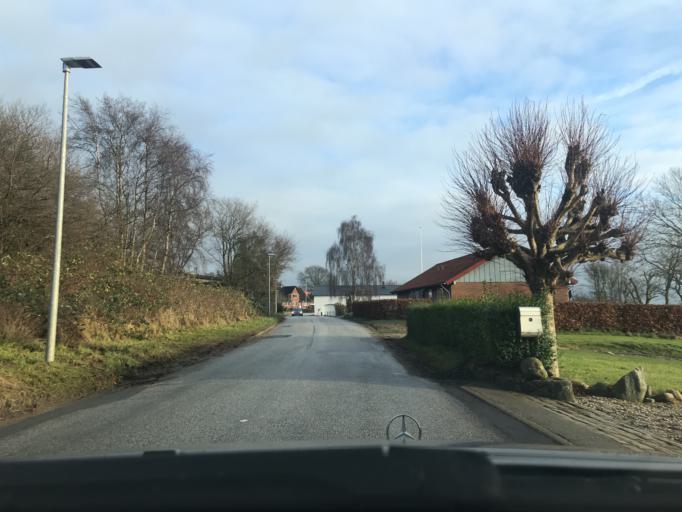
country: DK
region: South Denmark
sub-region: Sonderborg Kommune
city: Broager
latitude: 54.8779
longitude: 9.7018
